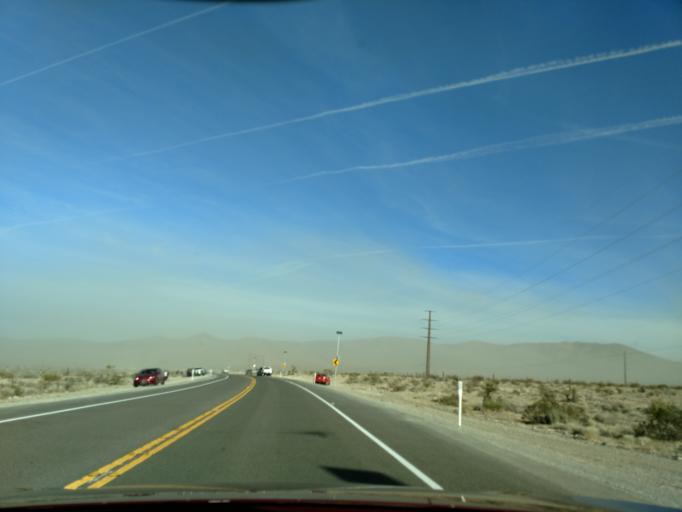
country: US
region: Nevada
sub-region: Nye County
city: Pahrump
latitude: 36.4306
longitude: -116.0714
